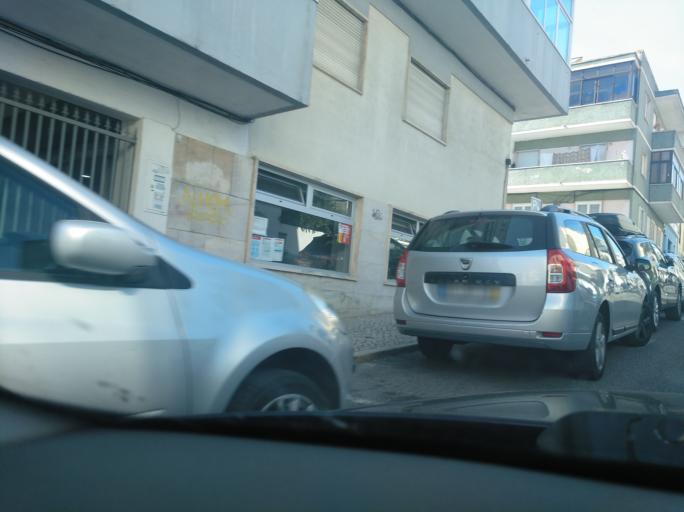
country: PT
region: Lisbon
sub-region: Oeiras
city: Alges
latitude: 38.7016
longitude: -9.2313
